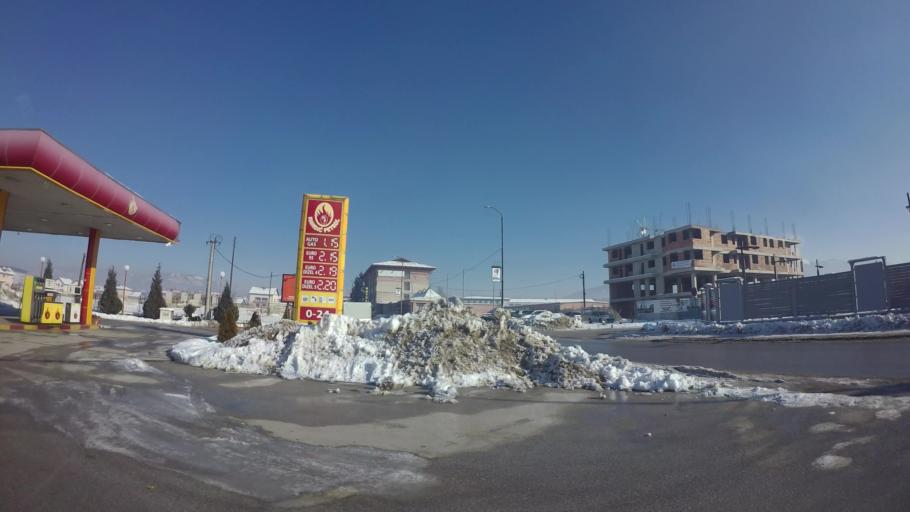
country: BA
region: Federation of Bosnia and Herzegovina
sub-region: Kanton Sarajevo
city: Sarajevo
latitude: 43.8176
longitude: 18.3552
